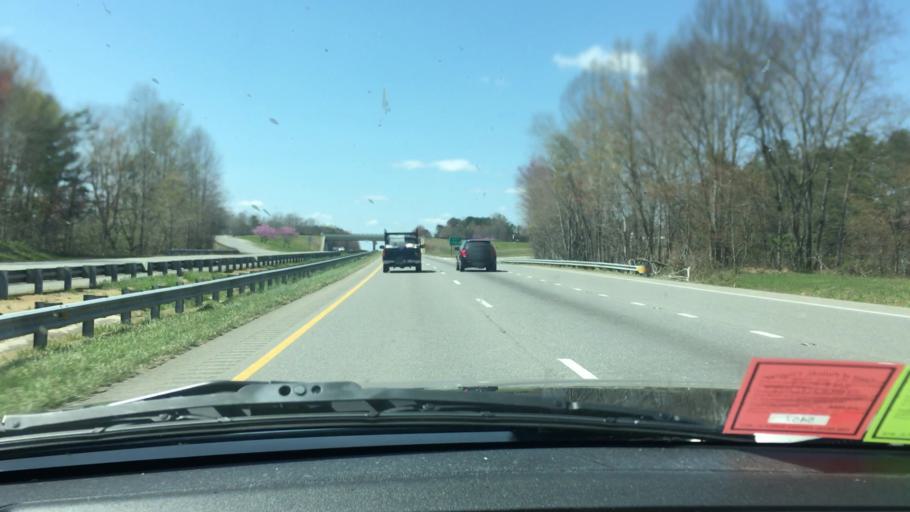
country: US
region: North Carolina
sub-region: Surry County
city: Pilot Mountain
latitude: 36.4057
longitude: -80.4963
